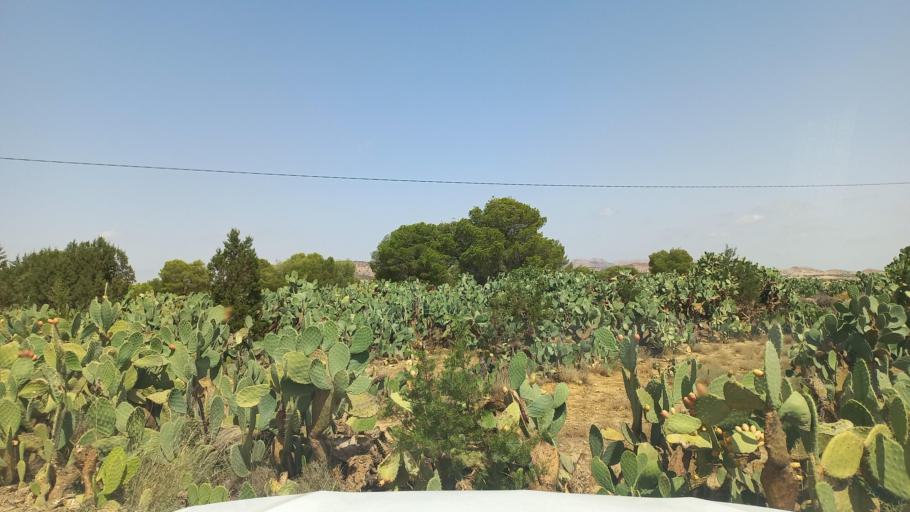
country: TN
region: Al Qasrayn
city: Sbiba
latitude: 35.3900
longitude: 8.9458
